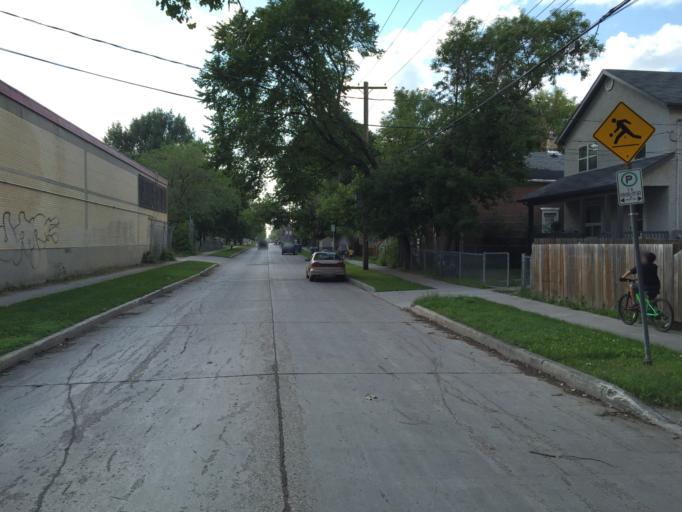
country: CA
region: Manitoba
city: Winnipeg
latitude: 49.9034
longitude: -97.1442
